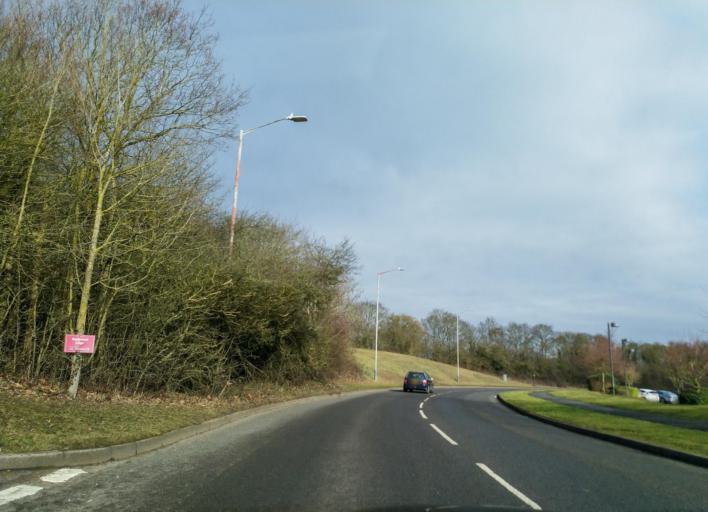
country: GB
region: England
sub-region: Warwickshire
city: Warwick
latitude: 52.2943
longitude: -1.6004
